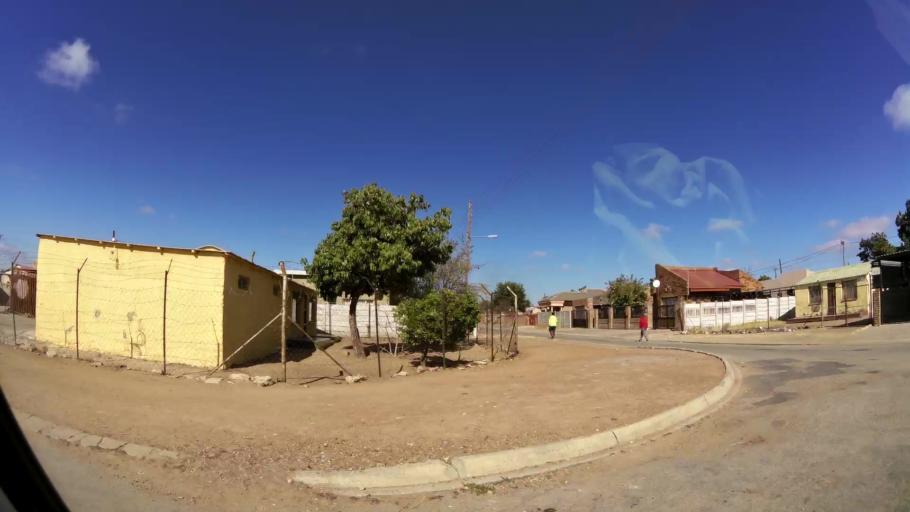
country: ZA
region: Limpopo
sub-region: Capricorn District Municipality
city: Polokwane
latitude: -23.8667
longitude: 29.3940
